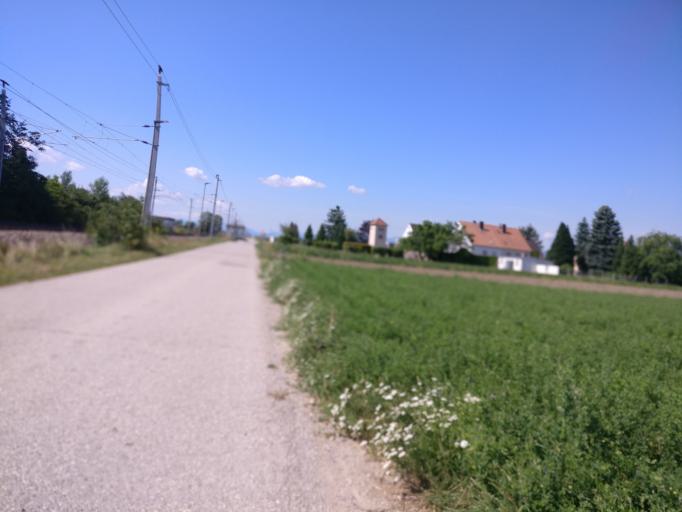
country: AT
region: Lower Austria
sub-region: Politischer Bezirk Wiener Neustadt
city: Zillingdorf
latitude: 47.8597
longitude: 16.3175
